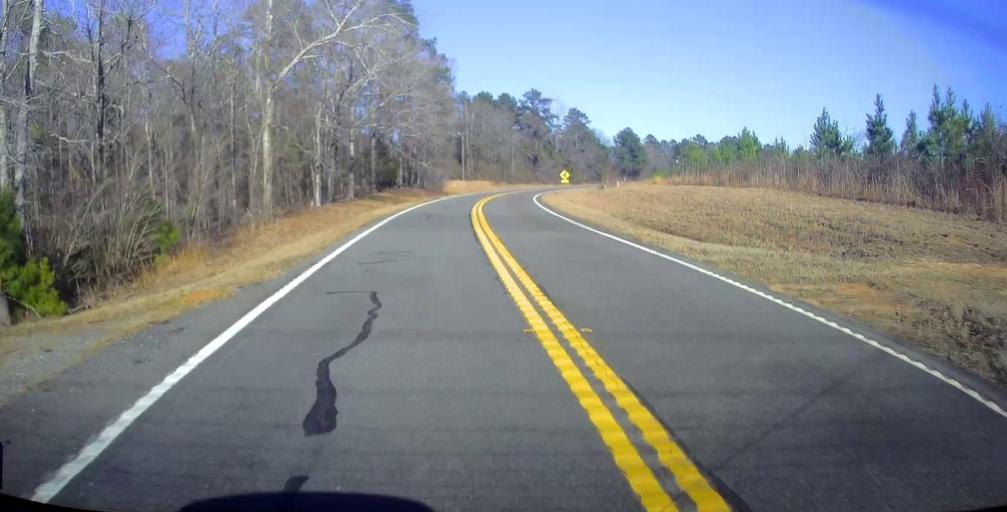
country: US
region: Georgia
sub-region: Talbot County
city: Talbotton
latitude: 32.6466
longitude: -84.4252
